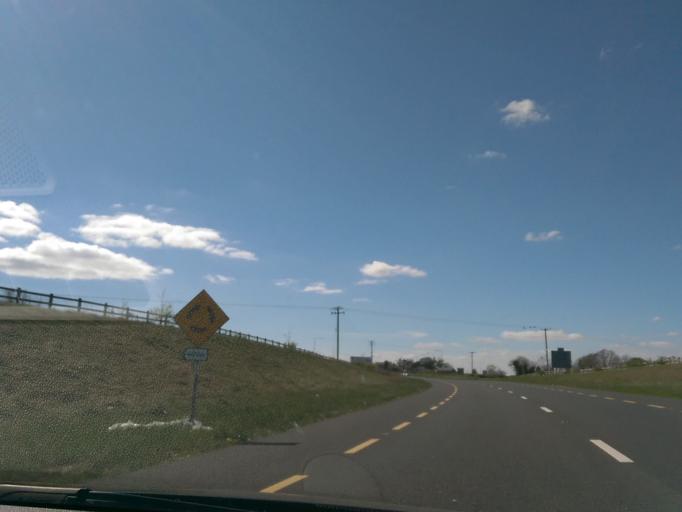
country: IE
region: Leinster
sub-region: Kildare
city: Athy
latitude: 52.9947
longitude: -6.9552
